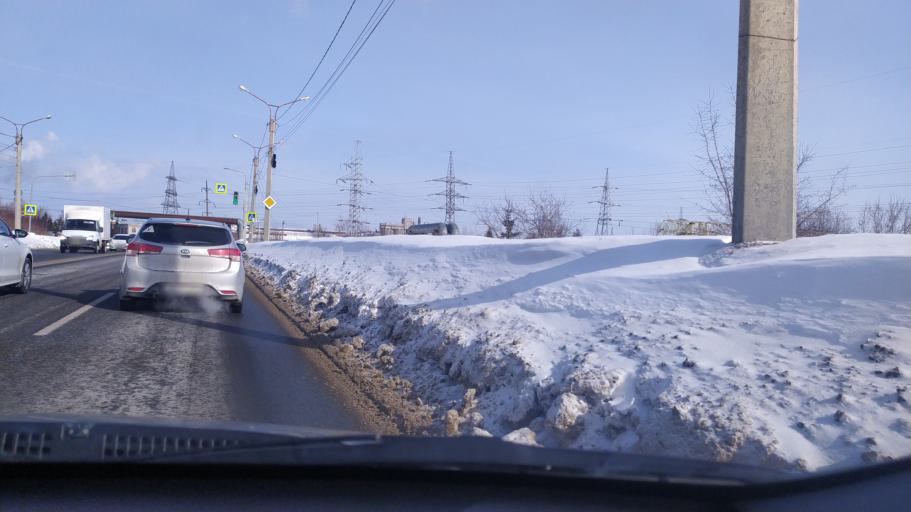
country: RU
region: Chuvashia
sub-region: Cheboksarskiy Rayon
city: Cheboksary
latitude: 56.1160
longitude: 47.3004
